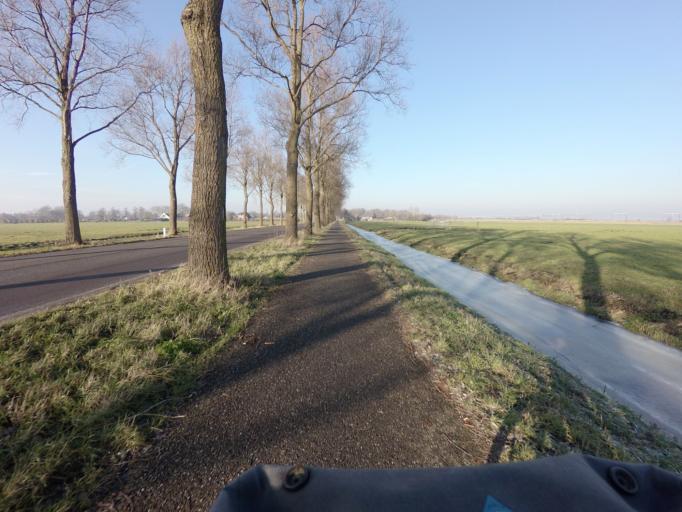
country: NL
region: North Holland
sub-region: Gemeente Amsterdam
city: Amsterdam-Zuidoost
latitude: 52.2639
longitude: 4.9844
